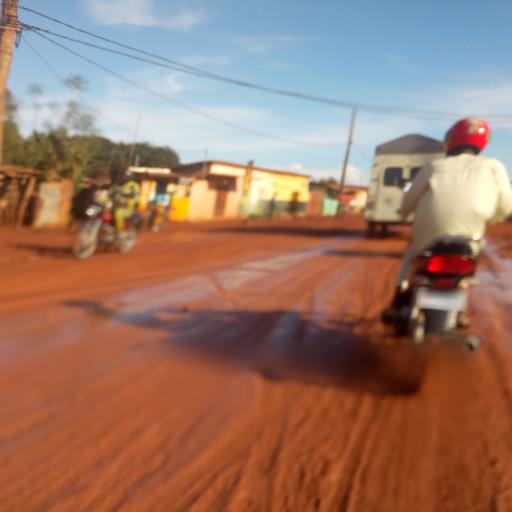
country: BJ
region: Atlantique
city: Hevie
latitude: 6.4149
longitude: 2.2636
